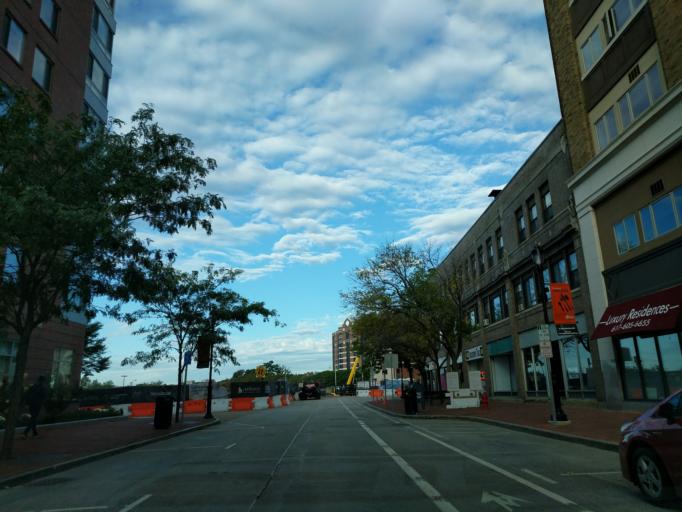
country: US
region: Massachusetts
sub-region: Middlesex County
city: Malden
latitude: 42.4272
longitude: -71.0713
